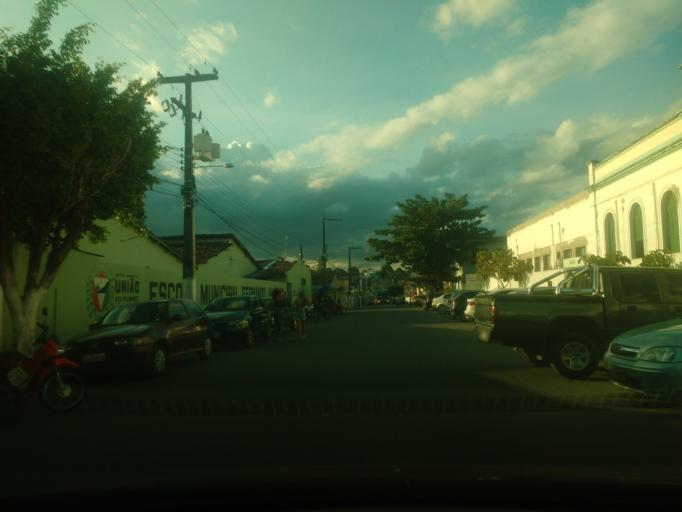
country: BR
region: Alagoas
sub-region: Uniao Dos Palmares
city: Uniao dos Palmares
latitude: -9.1596
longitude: -36.0290
